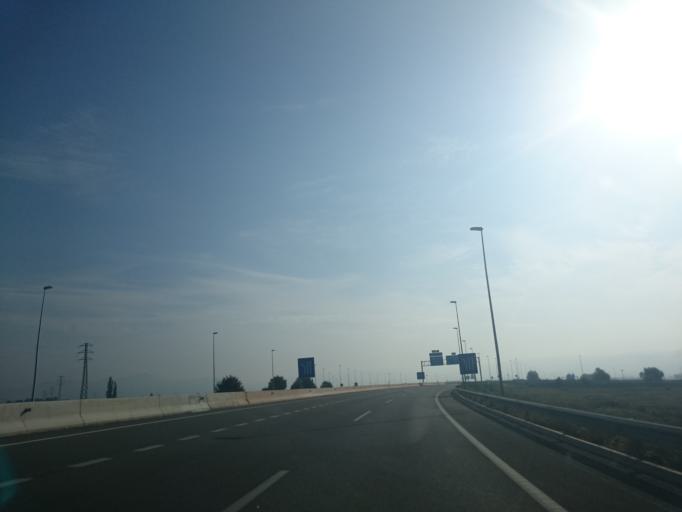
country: ES
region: Catalonia
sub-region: Provincia de Barcelona
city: Sant Fruitos de Bages
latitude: 41.7787
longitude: 1.8818
